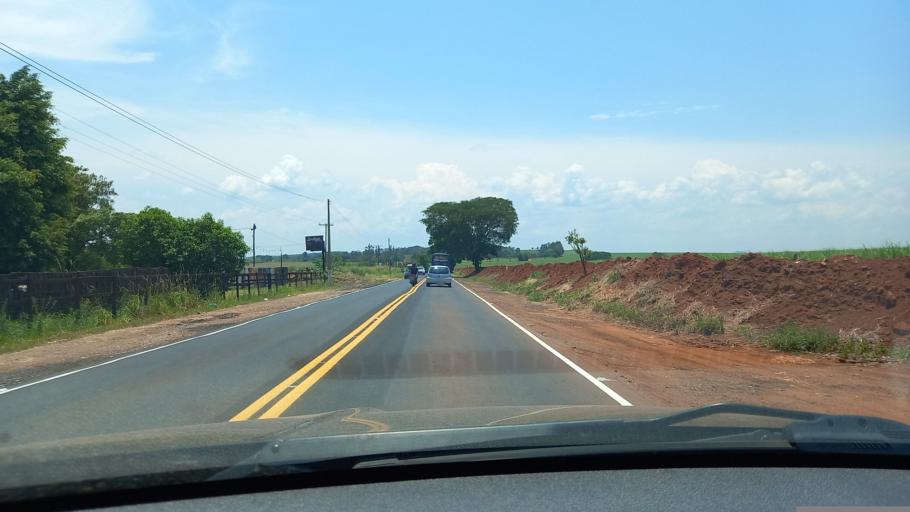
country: BR
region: Sao Paulo
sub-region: Moji-Guacu
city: Mogi-Gaucu
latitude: -22.3542
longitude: -46.9022
